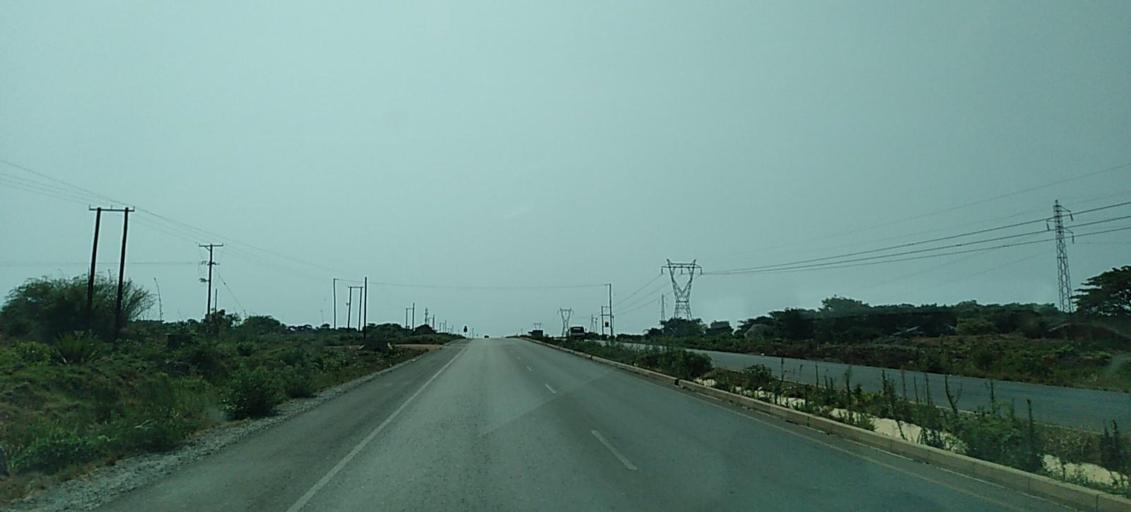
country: ZM
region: Copperbelt
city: Chingola
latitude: -12.5654
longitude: 27.8926
